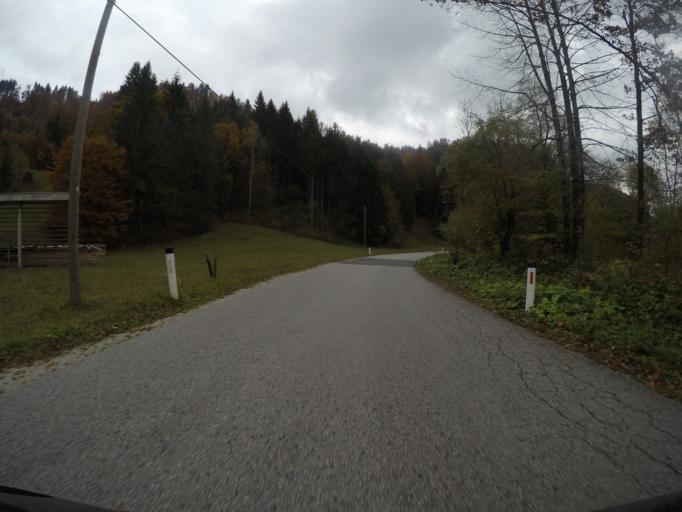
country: SI
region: Gorje
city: Zgornje Gorje
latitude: 46.3853
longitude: 14.0371
